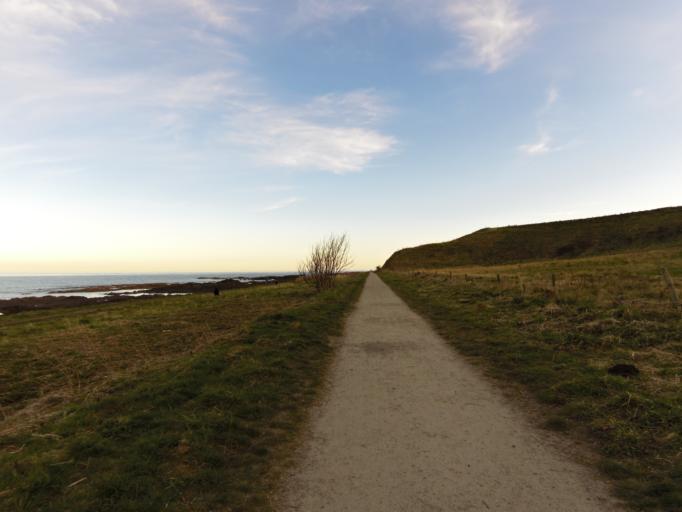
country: GB
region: Scotland
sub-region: Aberdeenshire
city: Inverbervie
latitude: 56.8381
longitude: -2.2758
